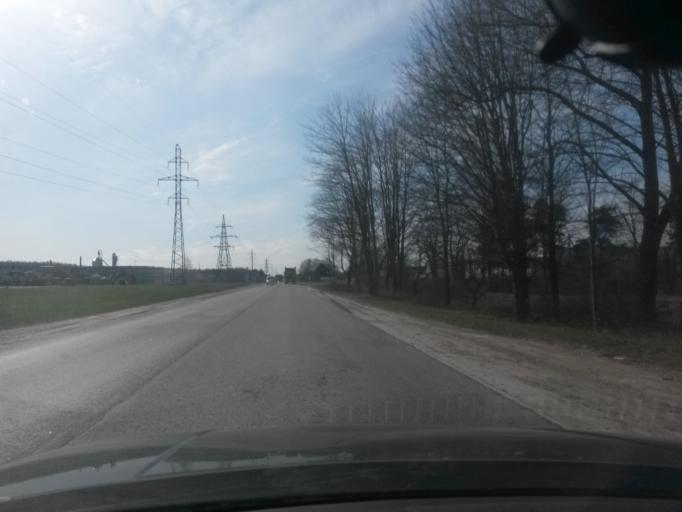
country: LV
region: Stopini
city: Ulbroka
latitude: 56.9136
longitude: 24.2497
